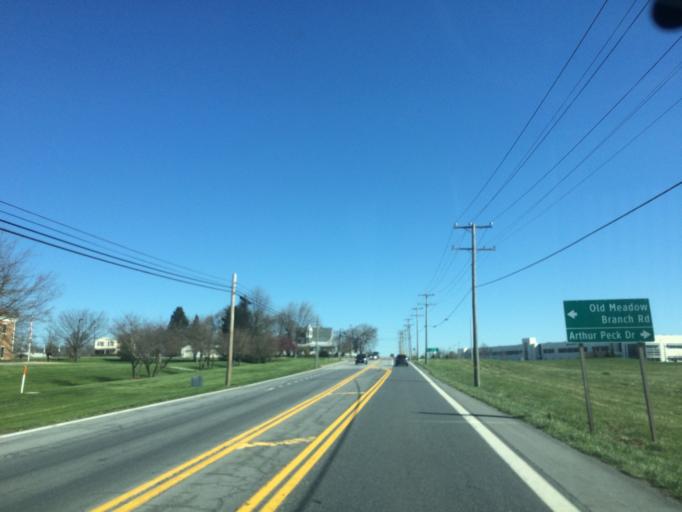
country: US
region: Maryland
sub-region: Carroll County
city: Westminster
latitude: 39.6107
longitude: -76.9979
